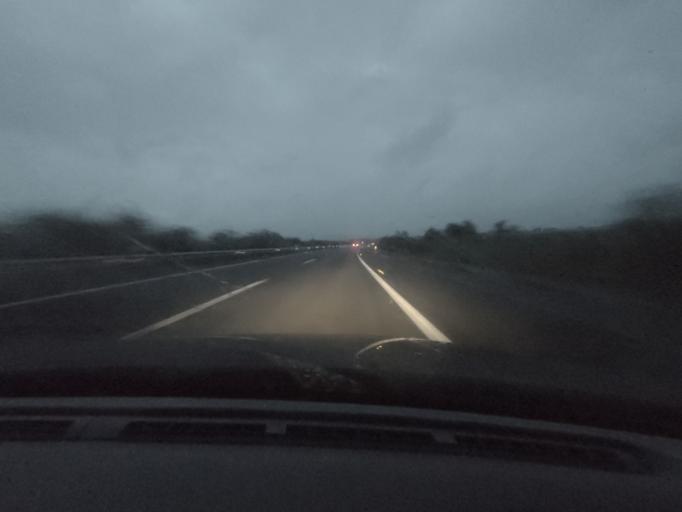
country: ES
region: Extremadura
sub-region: Provincia de Caceres
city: Aldea del Cano
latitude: 39.3517
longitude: -6.3419
